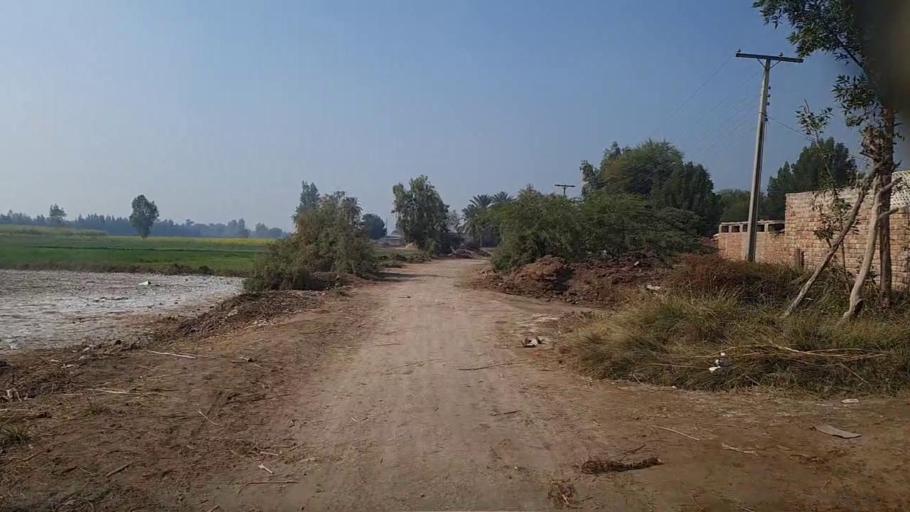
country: PK
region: Sindh
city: Khairpur
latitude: 27.9264
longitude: 69.6647
